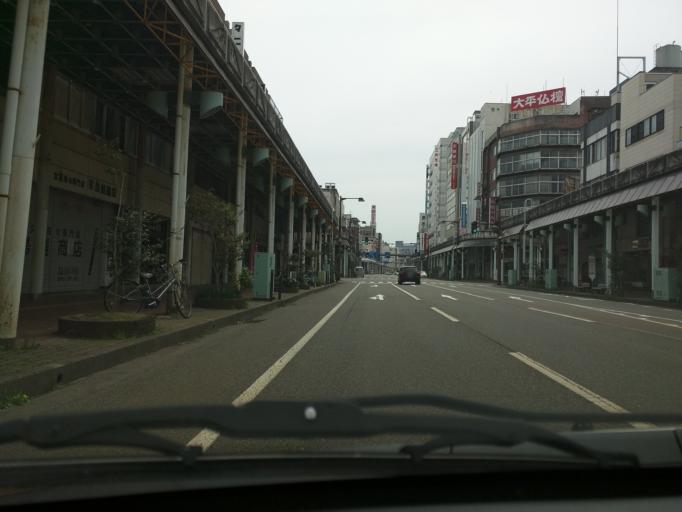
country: JP
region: Niigata
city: Nagaoka
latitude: 37.4496
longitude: 138.8515
